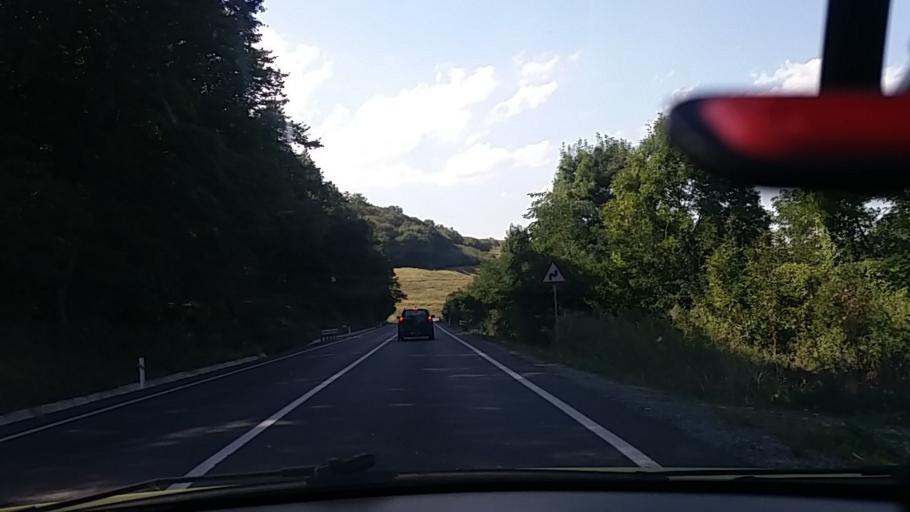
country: RO
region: Sibiu
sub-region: Comuna Slimnic
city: Slimnic
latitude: 45.9501
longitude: 24.1730
